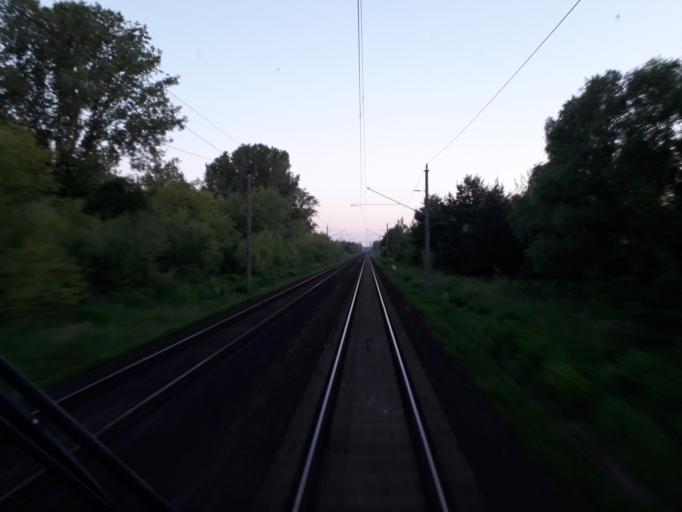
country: DE
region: Berlin
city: Stadtrandsiedlung Malchow
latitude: 52.5903
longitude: 13.4814
